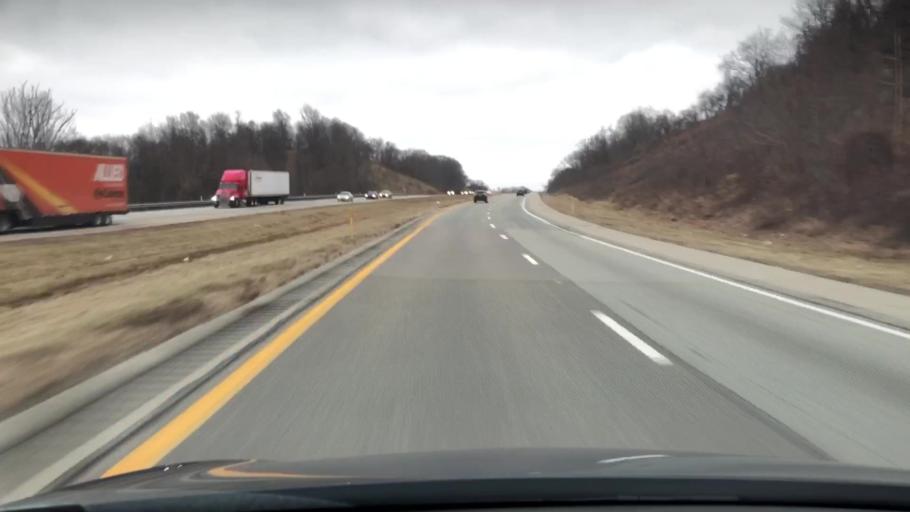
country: US
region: Pennsylvania
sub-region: Greene County
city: Morrisville
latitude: 39.8493
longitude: -80.1170
